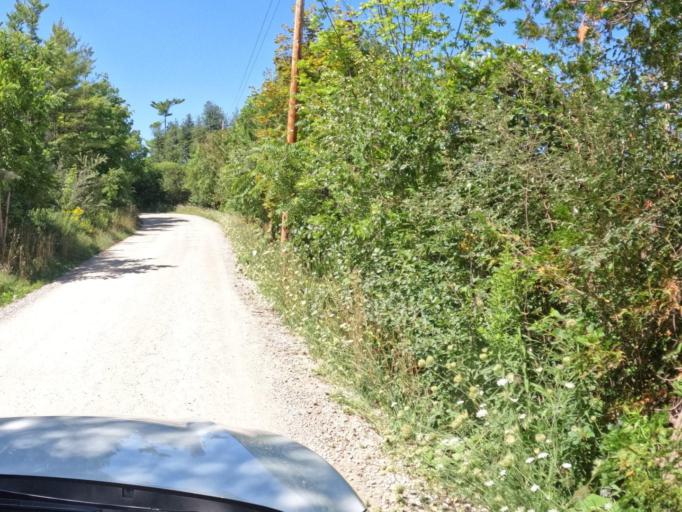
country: CA
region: Ontario
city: Cambridge
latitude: 43.4114
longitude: -80.2628
